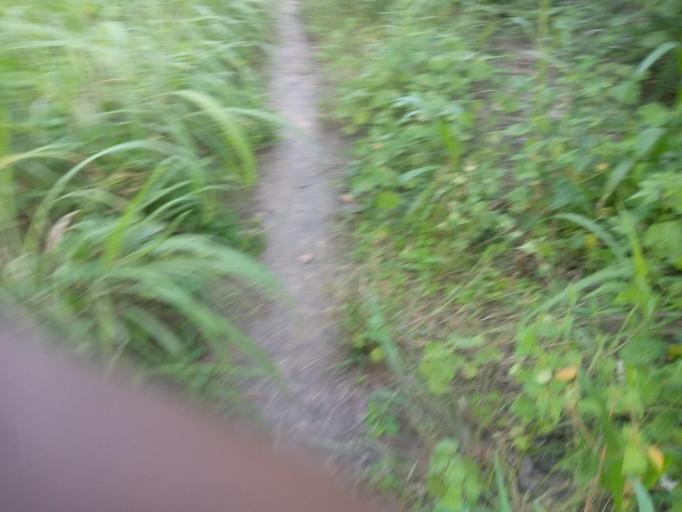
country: GM
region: Western
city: Gunjur
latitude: 13.0363
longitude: -16.7265
